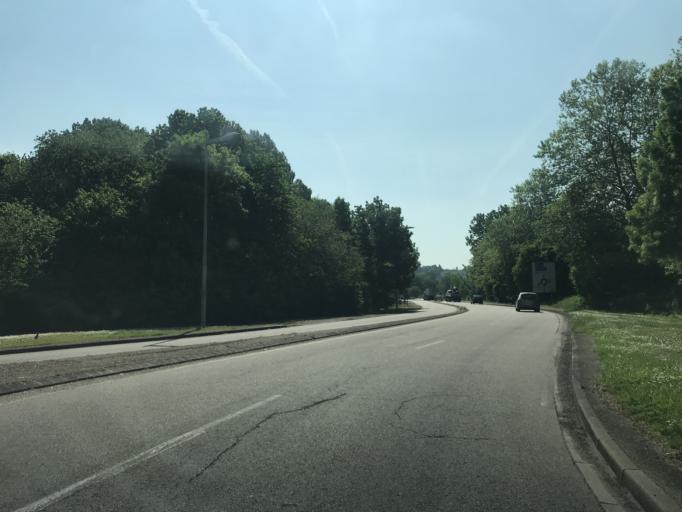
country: FR
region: Haute-Normandie
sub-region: Departement de la Seine-Maritime
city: Oissel
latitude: 49.3335
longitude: 1.0978
